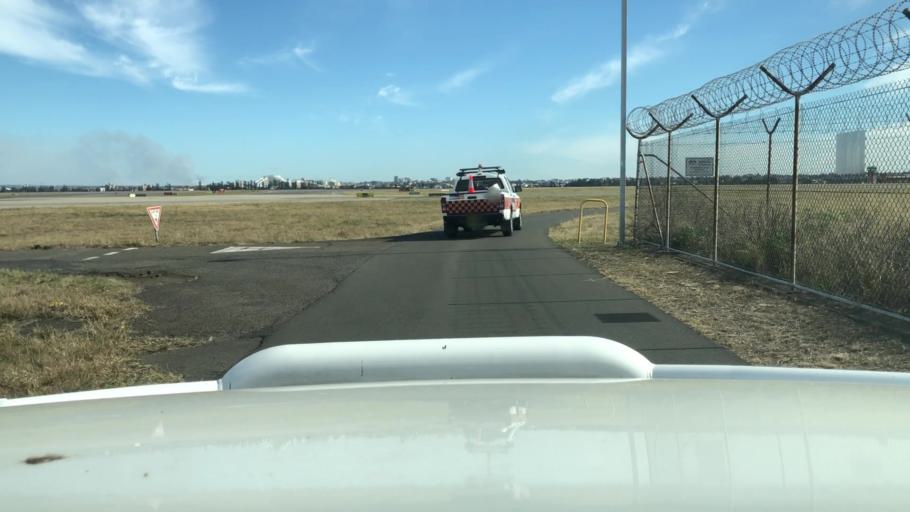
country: AU
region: New South Wales
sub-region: Botany Bay
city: Botany
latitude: -33.9504
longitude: 151.1815
